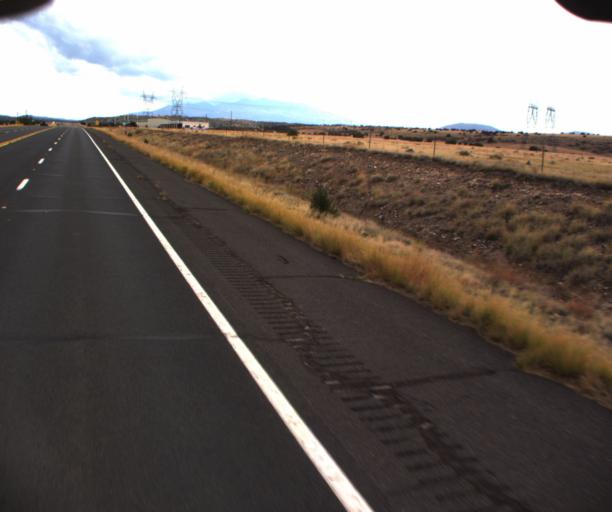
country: US
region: Arizona
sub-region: Coconino County
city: Flagstaff
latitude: 35.5436
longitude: -111.5385
